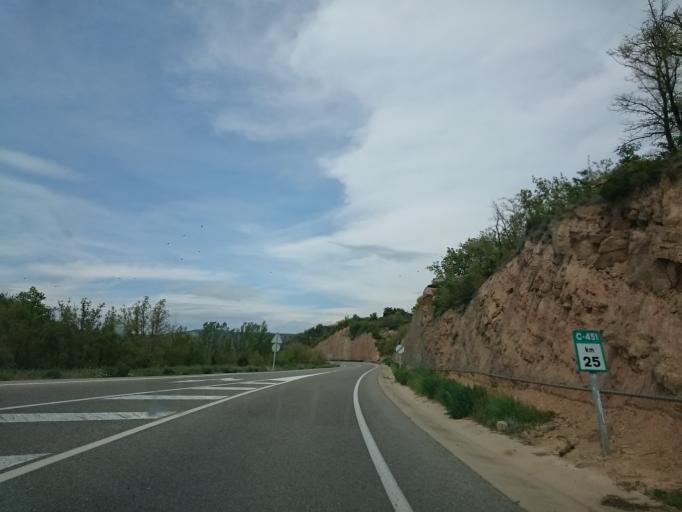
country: ES
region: Catalonia
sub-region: Provincia de Lleida
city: Tora de Riubregos
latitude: 41.8156
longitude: 1.3222
